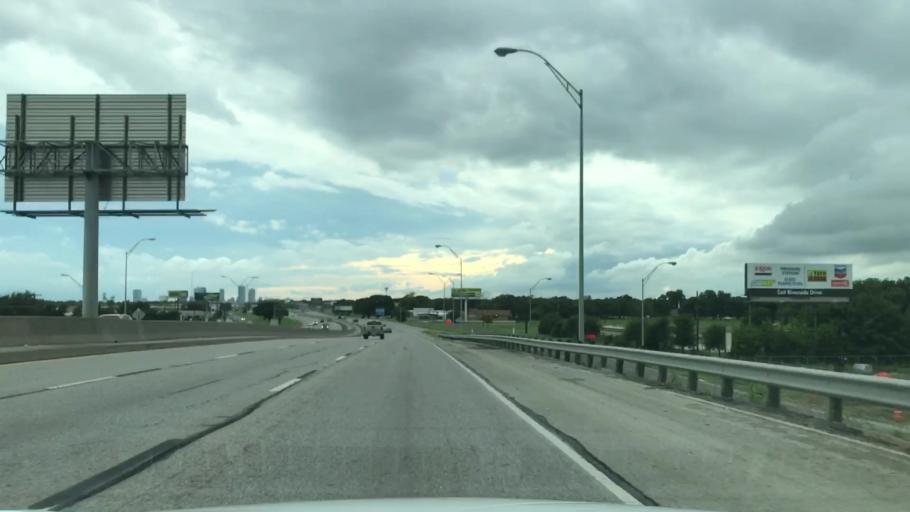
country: US
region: Texas
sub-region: Tarrant County
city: Haltom City
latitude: 32.7897
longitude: -97.2572
